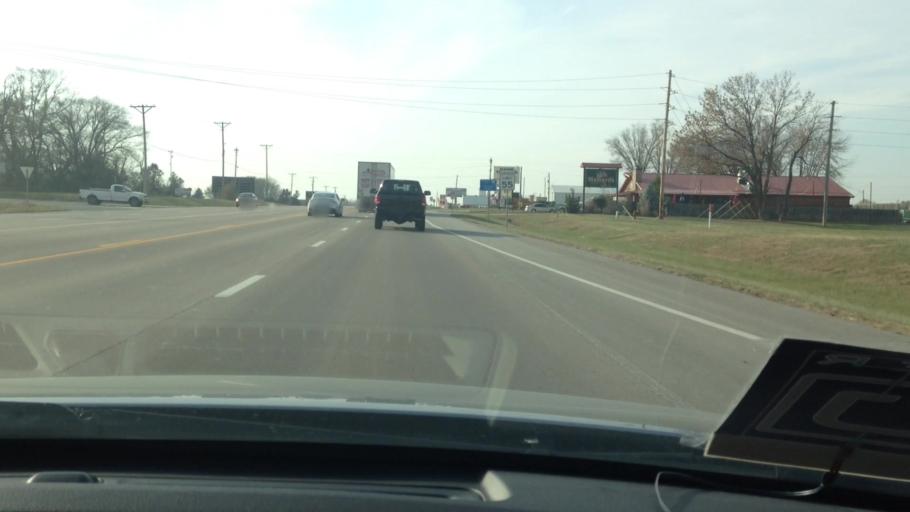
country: US
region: Missouri
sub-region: Henry County
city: Clinton
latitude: 38.3892
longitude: -93.7916
